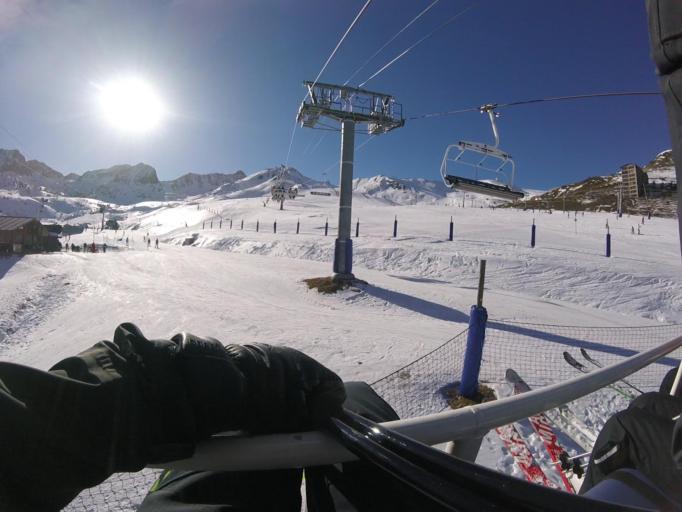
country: AD
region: Encamp
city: Pas de la Casa
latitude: 42.5389
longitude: 1.7344
